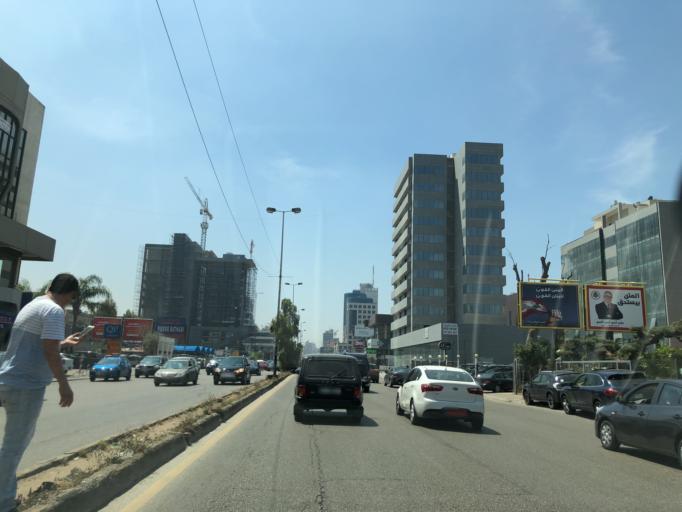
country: LB
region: Mont-Liban
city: Jdaidet el Matn
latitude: 33.8892
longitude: 35.5537
